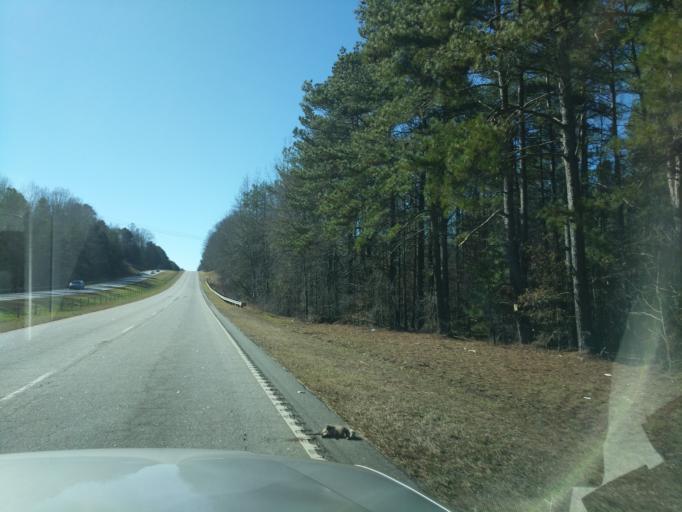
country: US
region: South Carolina
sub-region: Pickens County
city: Liberty
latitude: 34.7428
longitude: -82.7167
